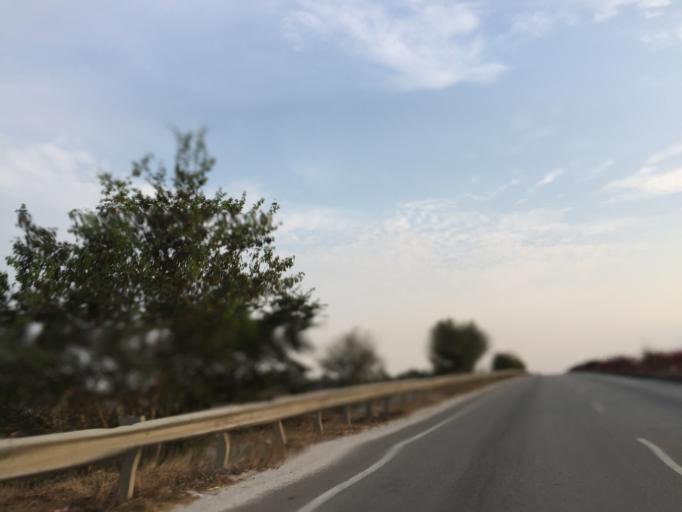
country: IN
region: Karnataka
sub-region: Chikkaballapur
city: Chik Ballapur
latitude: 13.4078
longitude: 77.7430
